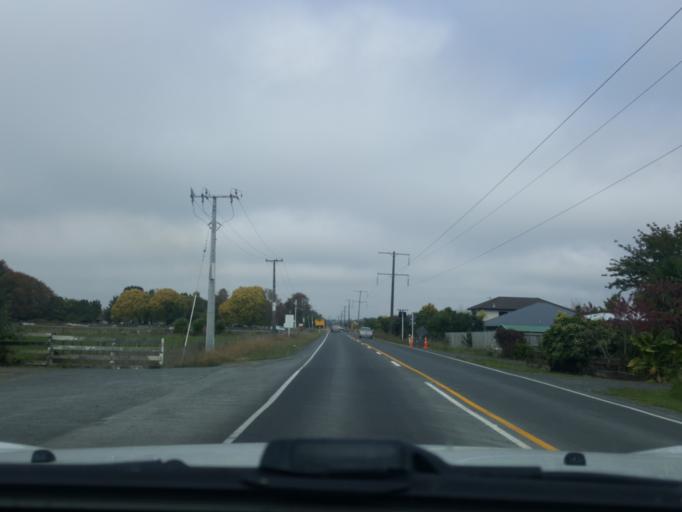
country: NZ
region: Waikato
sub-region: Hamilton City
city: Hamilton
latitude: -37.7333
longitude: 175.2874
